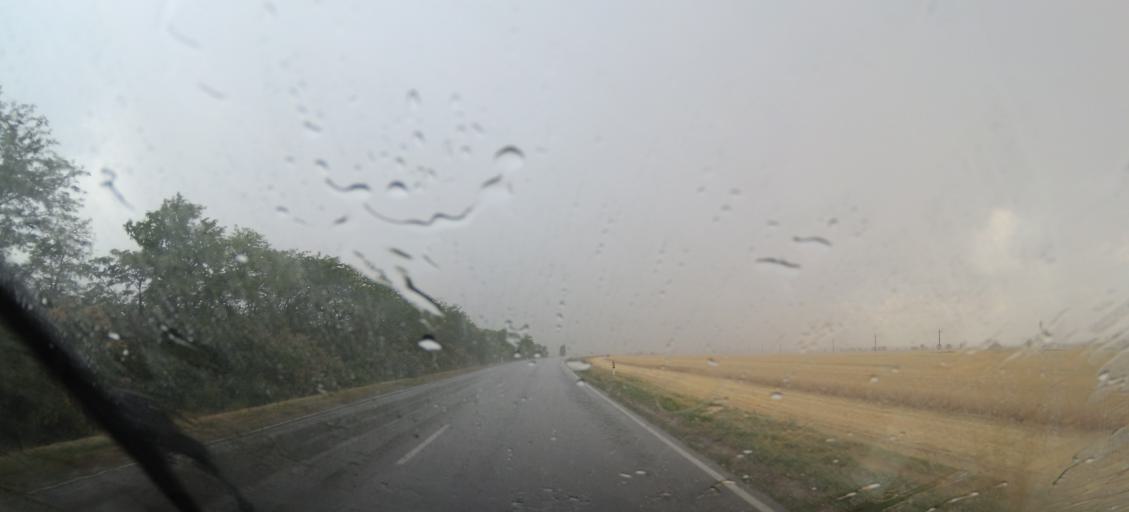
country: RU
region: Rostov
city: Proletarsk
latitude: 46.6697
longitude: 41.6923
